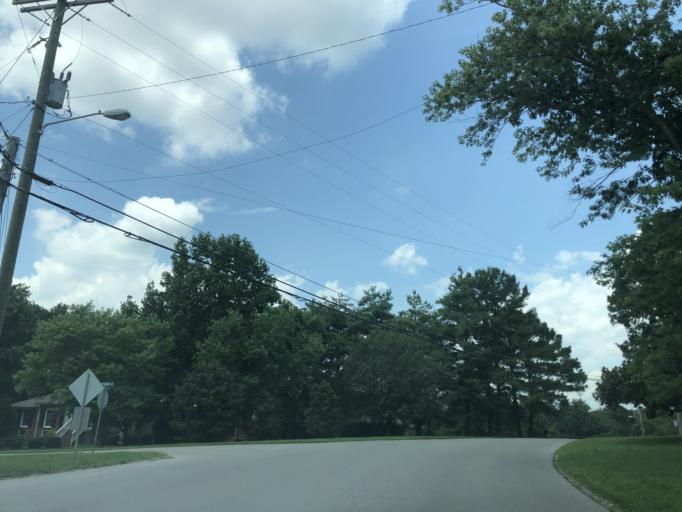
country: US
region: Tennessee
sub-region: Williamson County
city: Brentwood Estates
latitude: 36.0100
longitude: -86.7384
